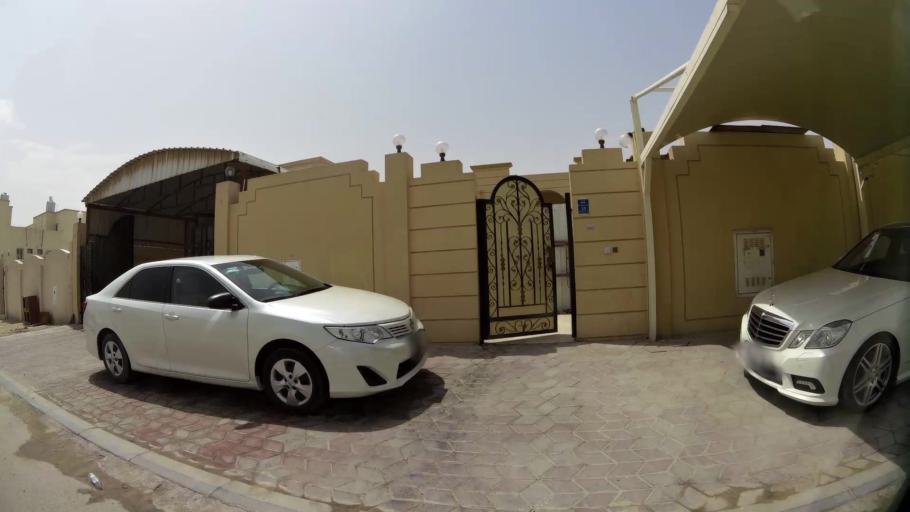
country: QA
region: Baladiyat ar Rayyan
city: Ar Rayyan
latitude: 25.2271
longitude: 51.4120
